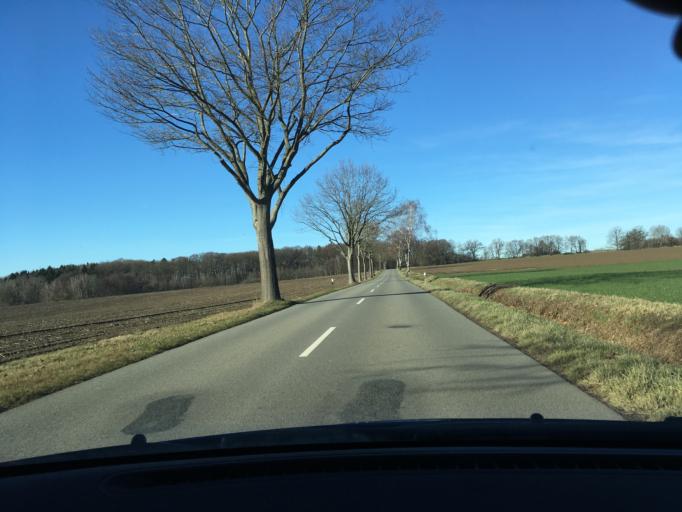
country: DE
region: Lower Saxony
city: Schwienau
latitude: 52.9702
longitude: 10.4555
